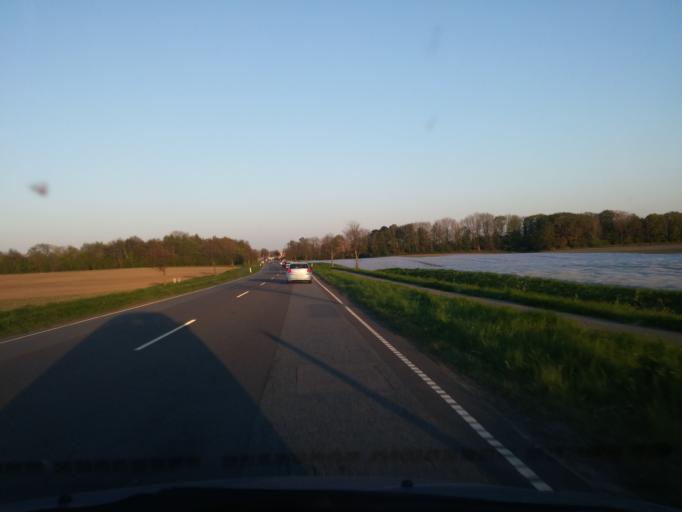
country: DK
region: South Denmark
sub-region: Nyborg Kommune
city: Nyborg
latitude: 55.3226
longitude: 10.7716
